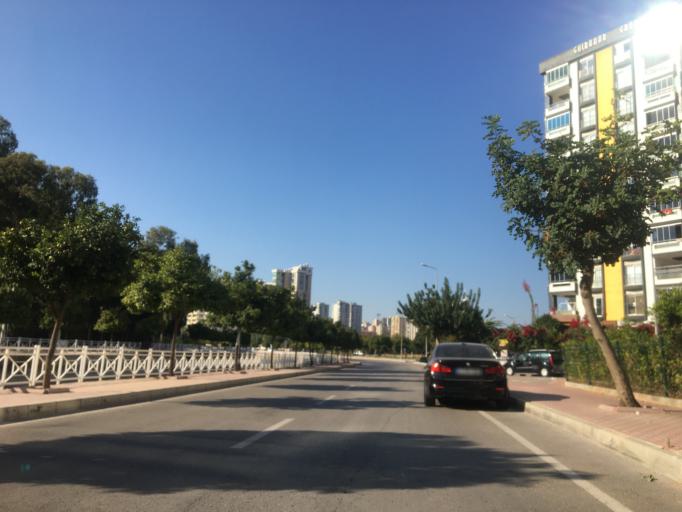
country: TR
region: Adana
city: Seyhan
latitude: 37.0278
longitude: 35.2722
